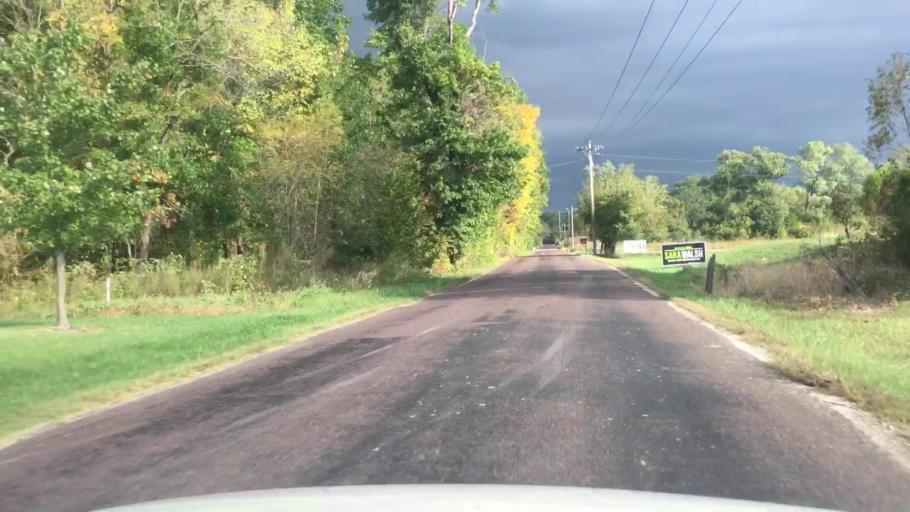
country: US
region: Missouri
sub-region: Boone County
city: Columbia
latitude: 38.8633
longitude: -92.3739
